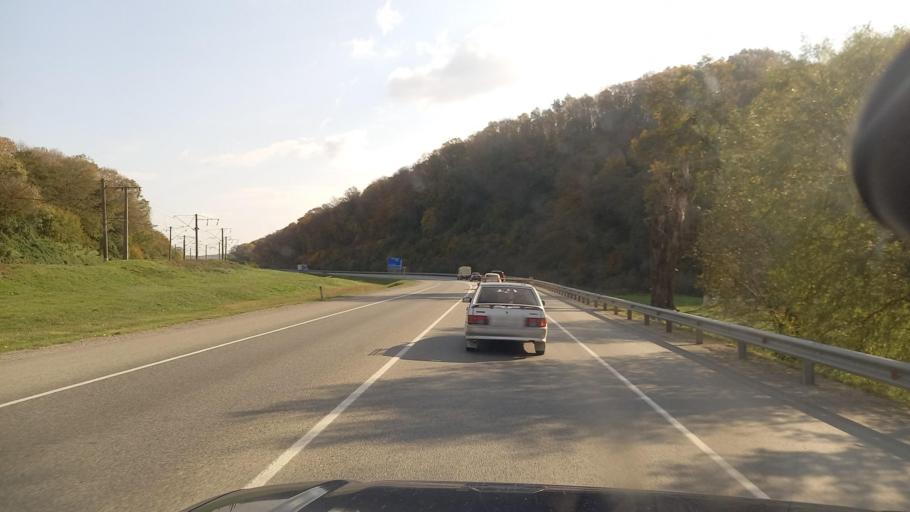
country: RU
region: Krasnodarskiy
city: Krymsk
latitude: 44.8707
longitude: 37.8966
